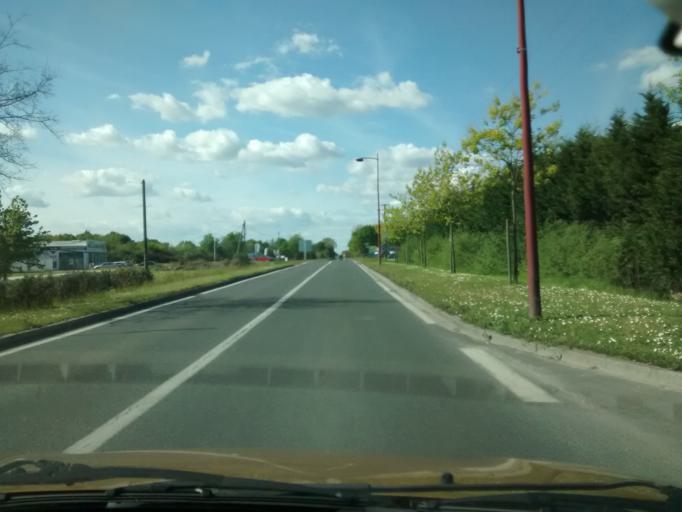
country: FR
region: Pays de la Loire
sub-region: Departement de la Loire-Atlantique
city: Geneston
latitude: 47.0672
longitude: -1.5184
